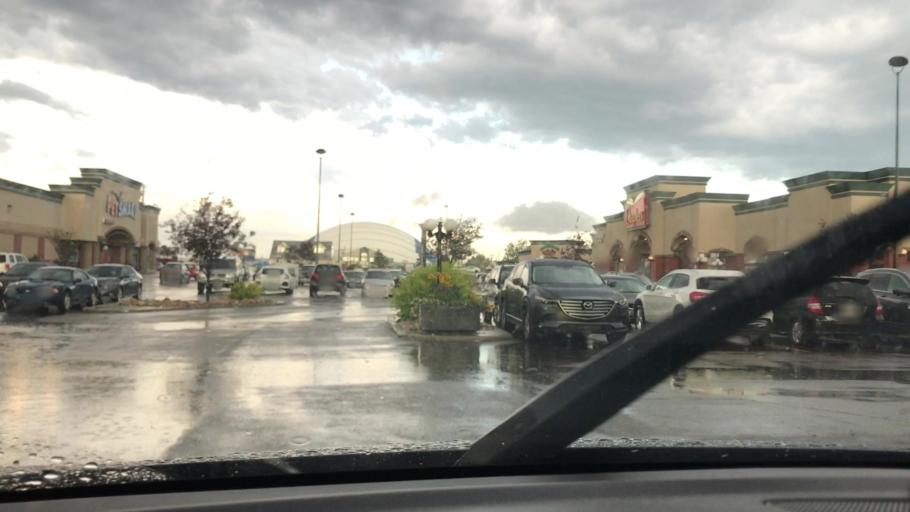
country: CA
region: Alberta
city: Edmonton
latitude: 53.4645
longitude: -113.4950
